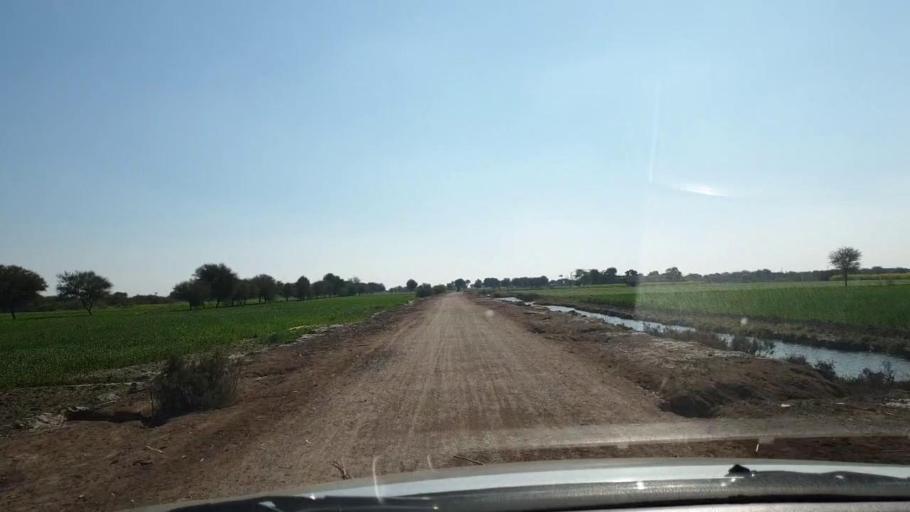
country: PK
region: Sindh
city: Jhol
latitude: 25.9193
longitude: 68.9587
